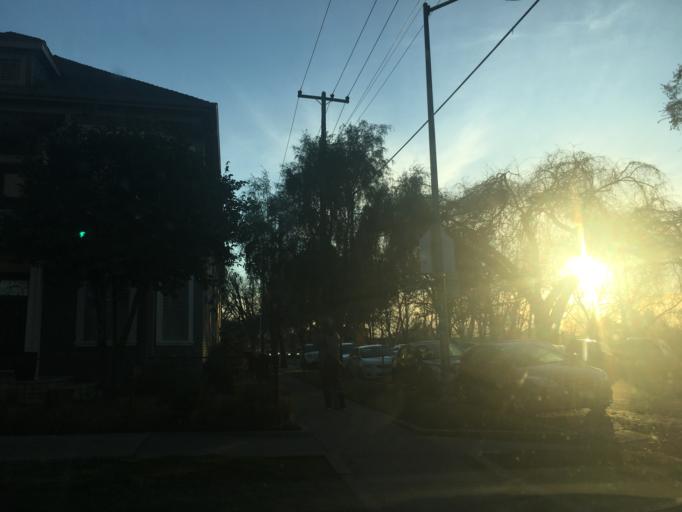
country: US
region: California
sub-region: Sacramento County
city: Sacramento
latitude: 38.5688
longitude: -121.5013
